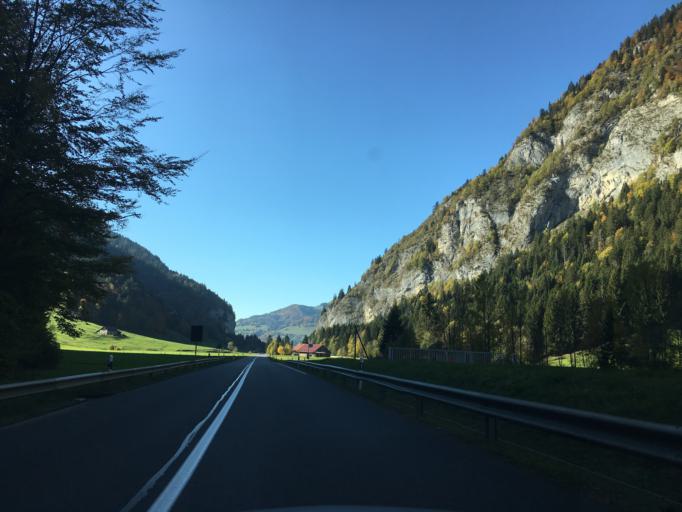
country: CH
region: Fribourg
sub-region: Gruyere District
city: Charmey
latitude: 46.6070
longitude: 7.1974
